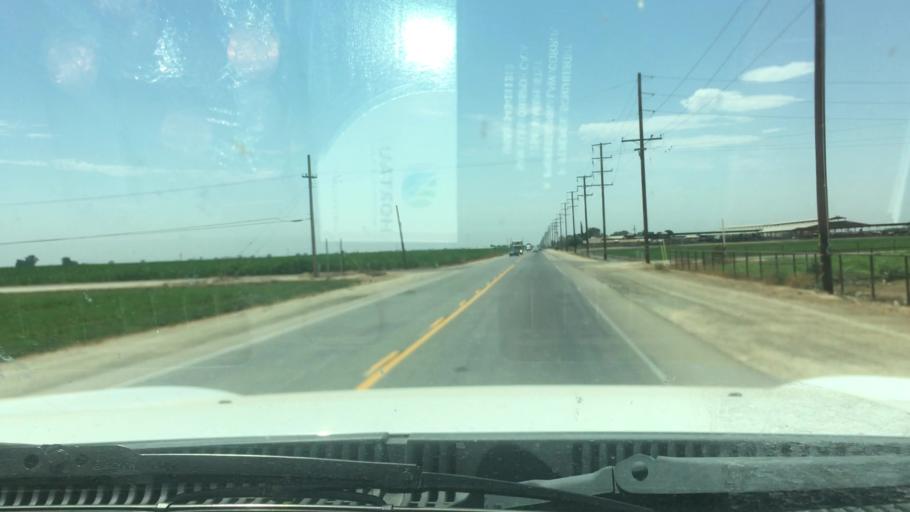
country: US
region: California
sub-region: Tulare County
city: Tipton
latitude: 36.0658
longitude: -119.2582
